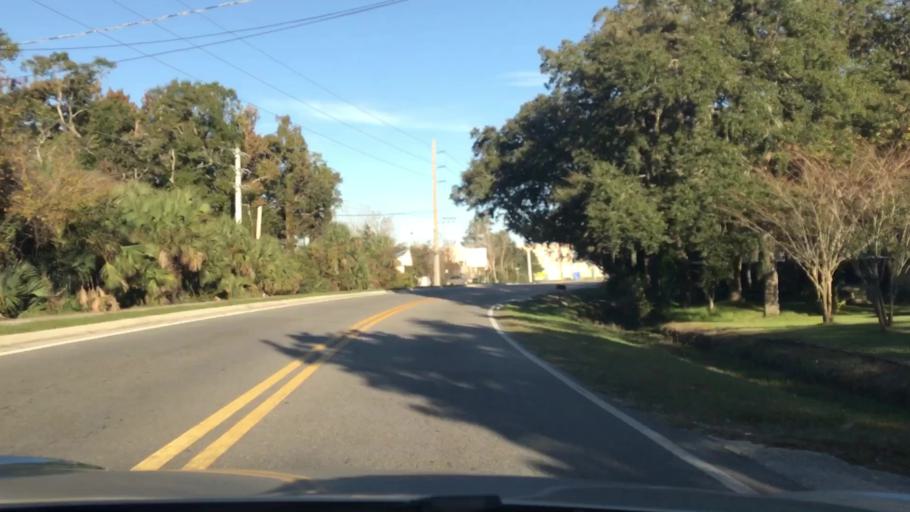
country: US
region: Florida
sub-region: Saint Johns County
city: Villano Beach
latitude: 29.9392
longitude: -81.3434
